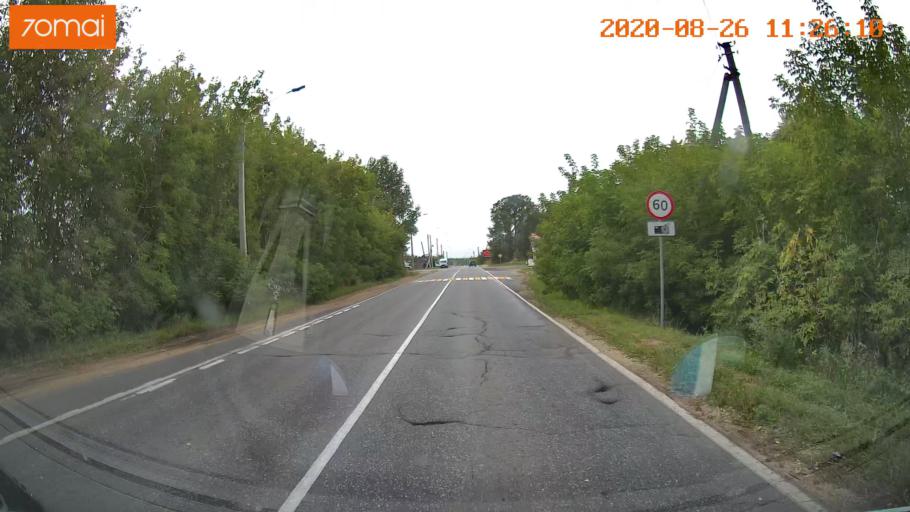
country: RU
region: Rjazan
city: Shilovo
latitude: 54.3358
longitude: 40.9532
